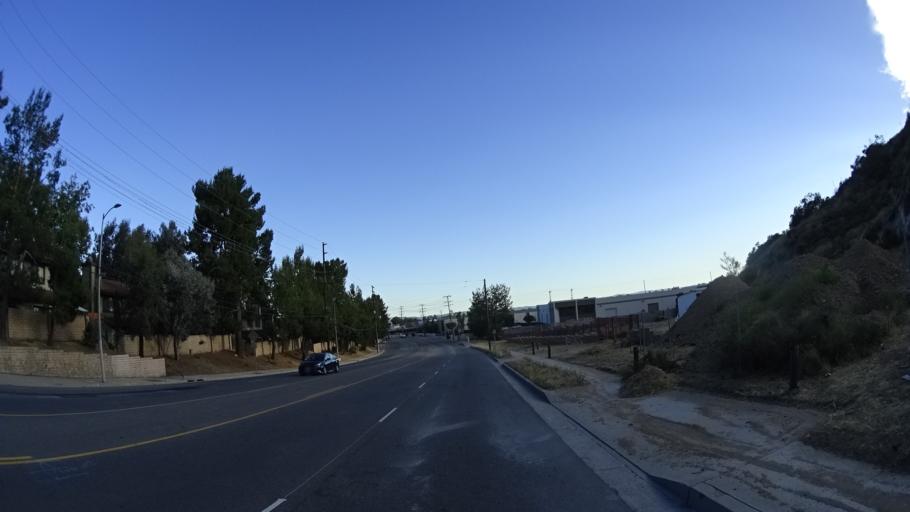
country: US
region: California
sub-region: Los Angeles County
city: North Hollywood
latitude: 34.2417
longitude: -118.3673
